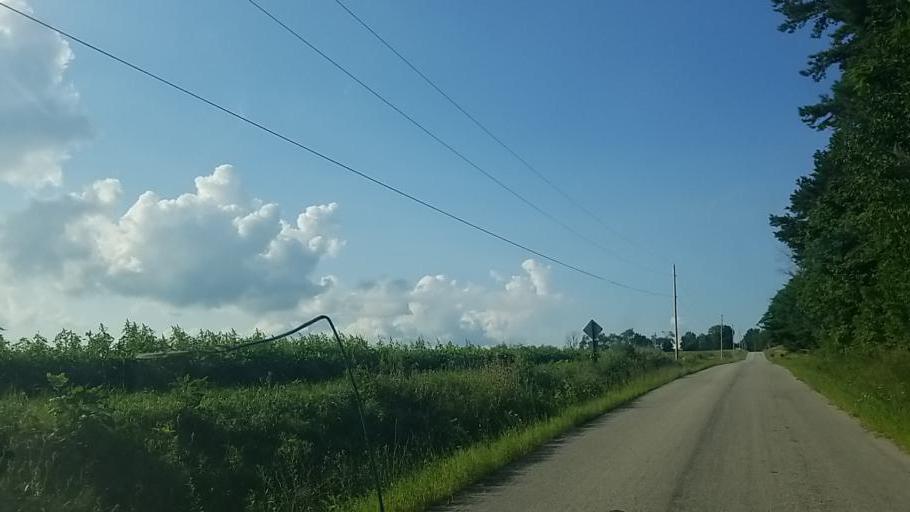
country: US
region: Ohio
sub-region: Wayne County
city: West Salem
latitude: 40.8865
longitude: -82.0333
